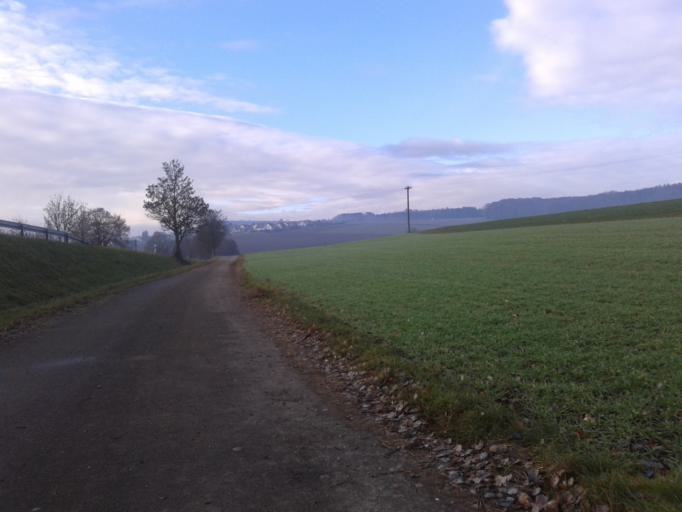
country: DE
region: Baden-Wuerttemberg
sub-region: Tuebingen Region
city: Erbach
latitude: 48.3884
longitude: 9.9128
